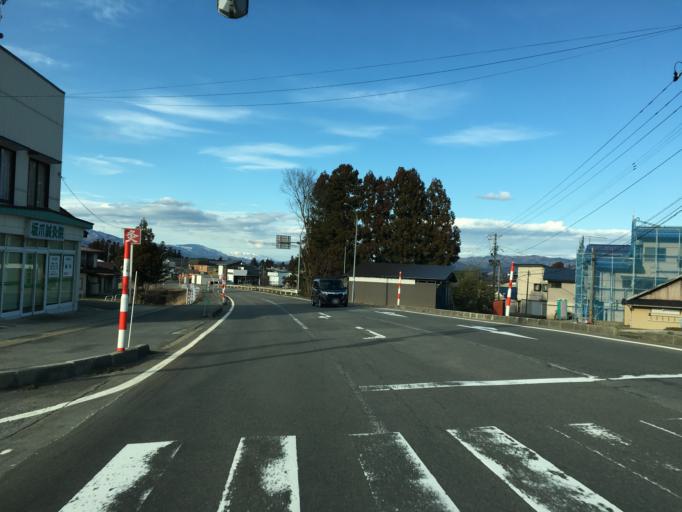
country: JP
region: Yamagata
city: Nagai
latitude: 38.0389
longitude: 139.9900
